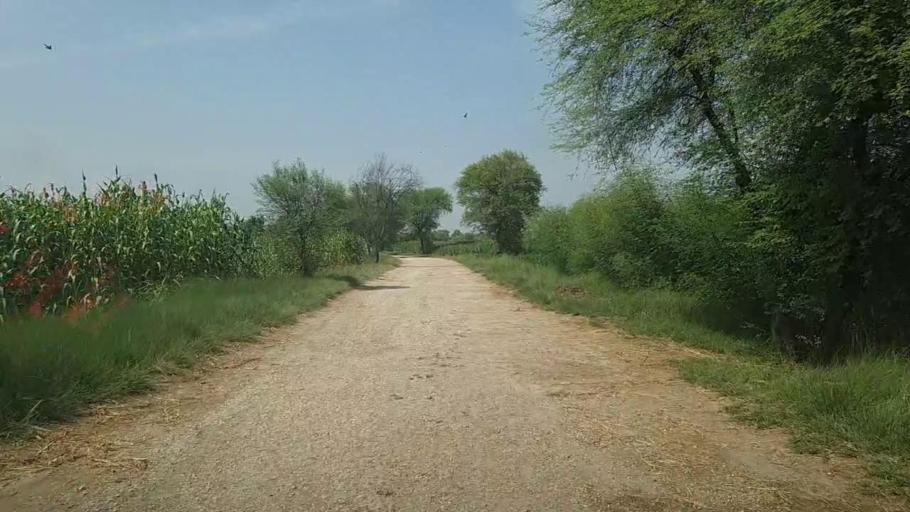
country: PK
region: Sindh
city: Ubauro
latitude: 28.1771
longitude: 69.8150
